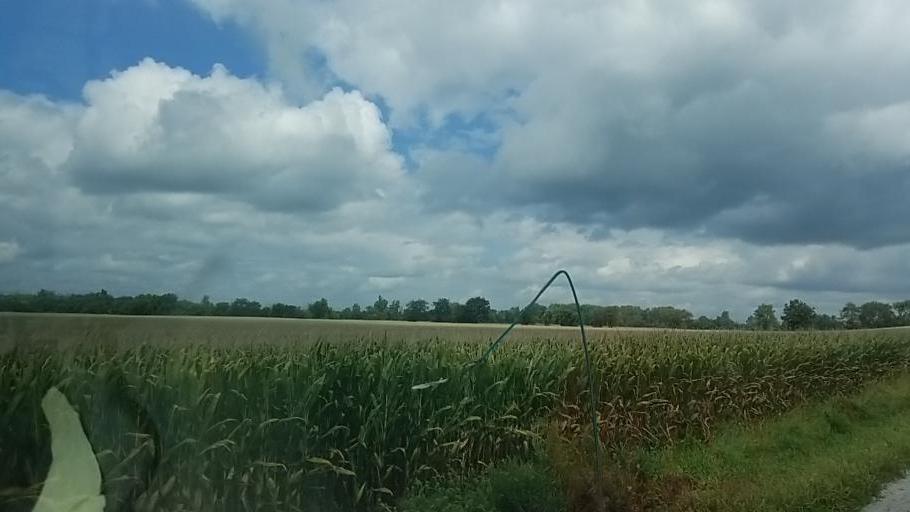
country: US
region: Ohio
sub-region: Clark County
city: South Charleston
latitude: 39.8258
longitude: -83.7198
